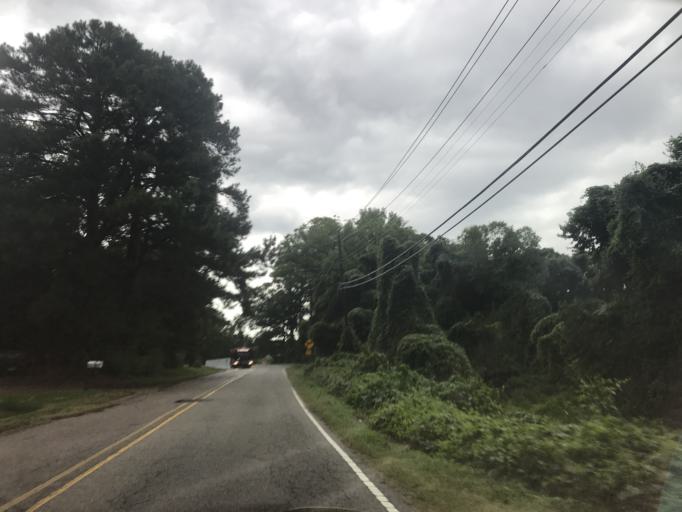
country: US
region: North Carolina
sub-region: Wake County
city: Raleigh
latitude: 35.7480
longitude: -78.6518
